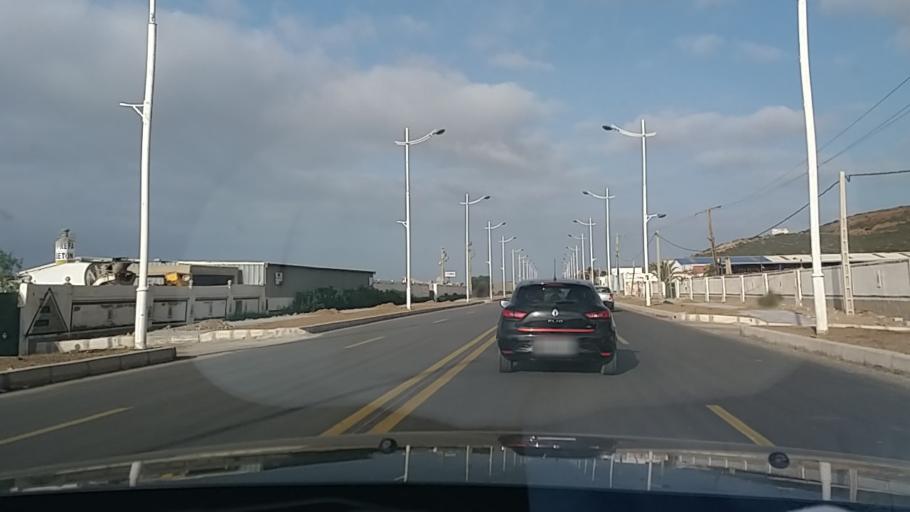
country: MA
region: Tanger-Tetouan
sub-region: Tetouan
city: Martil
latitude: 35.5758
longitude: -5.3116
